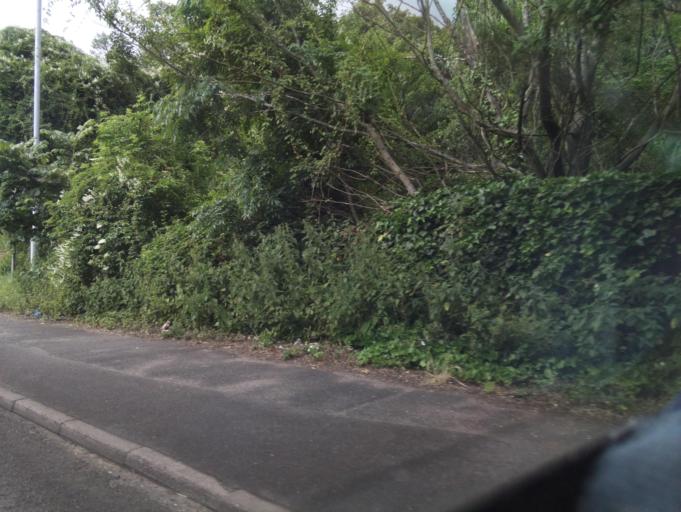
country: GB
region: England
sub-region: Dudley
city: Kingswinford
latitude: 52.5193
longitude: -2.1754
